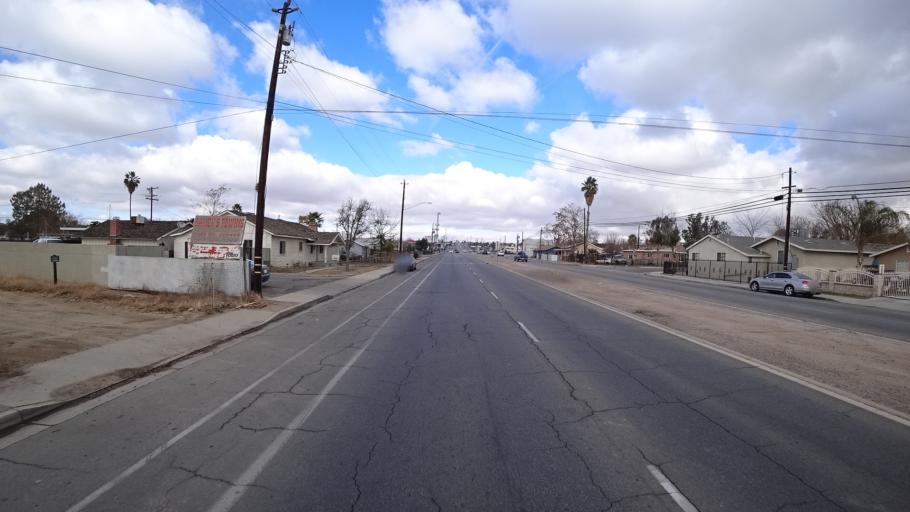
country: US
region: California
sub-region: Kern County
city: Bakersfield
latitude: 35.3663
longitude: -118.9676
